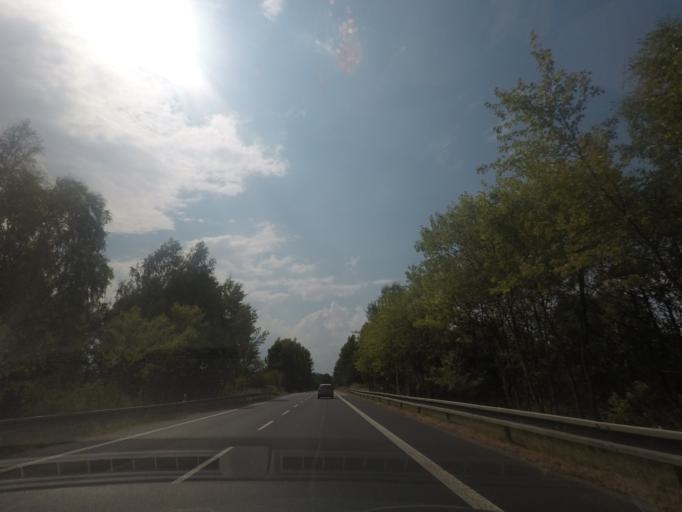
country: CZ
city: Brniste
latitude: 50.7724
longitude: 14.6883
